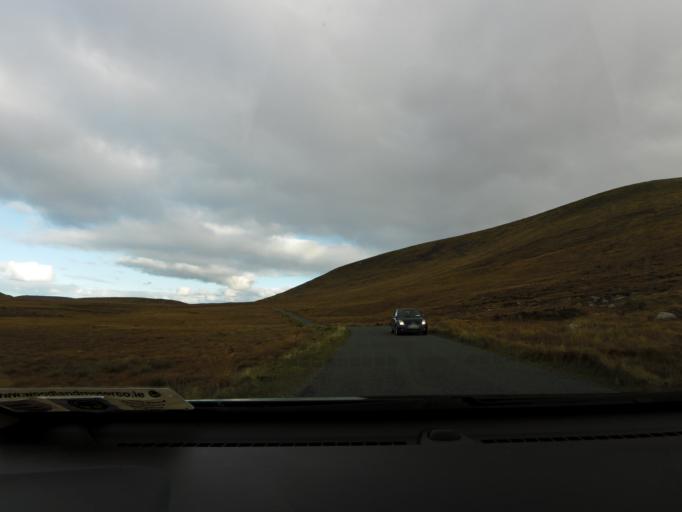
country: IE
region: Connaught
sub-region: Maigh Eo
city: Belmullet
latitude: 53.9301
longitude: -10.0079
